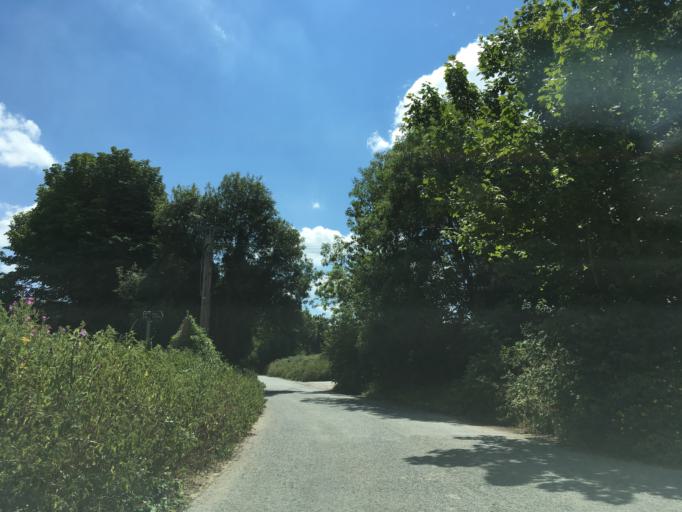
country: GB
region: England
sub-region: Gloucestershire
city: Shurdington
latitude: 51.8453
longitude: -2.1271
